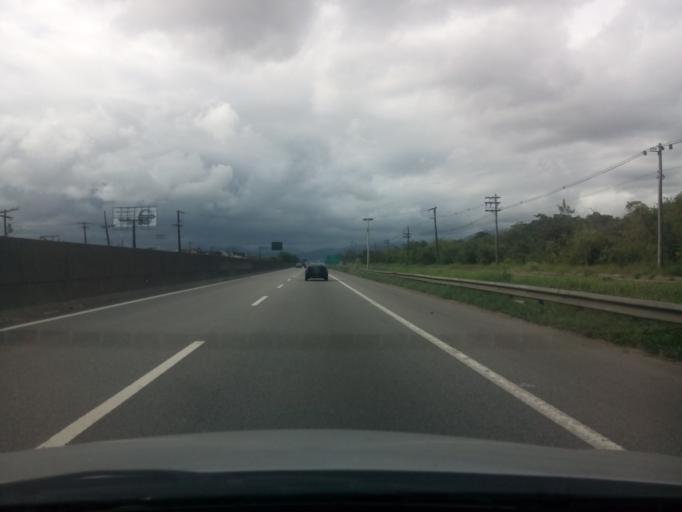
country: BR
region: Sao Paulo
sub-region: Guaruja
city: Guaruja
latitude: -23.9607
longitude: -46.2734
